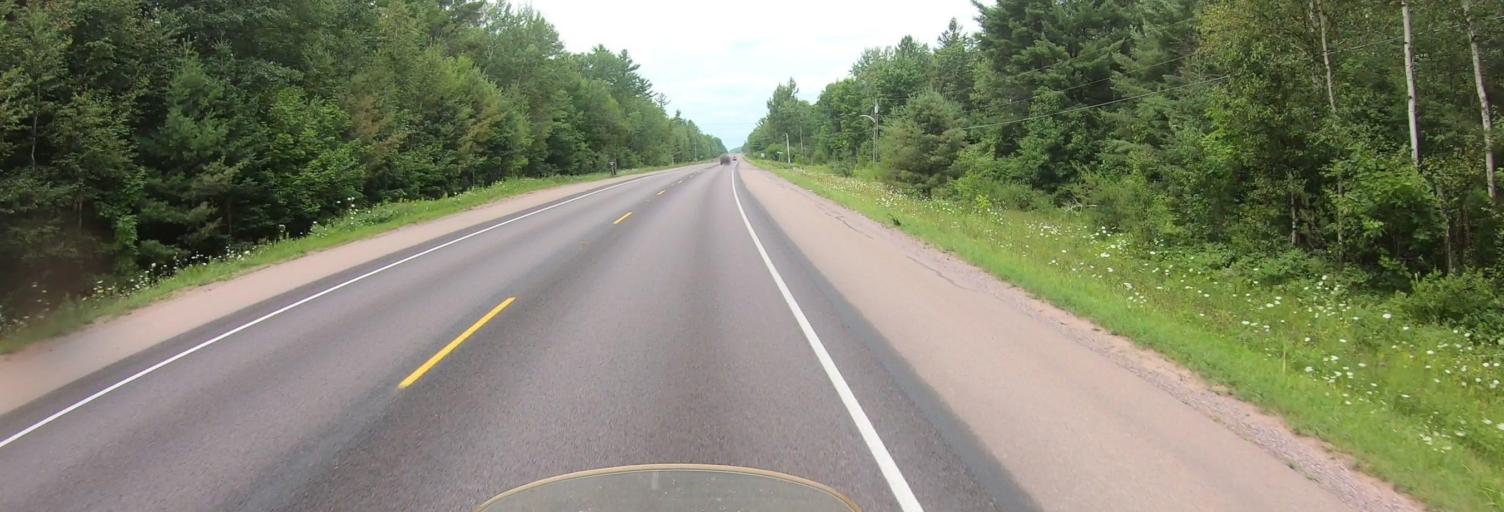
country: US
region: Michigan
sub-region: Marquette County
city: Marquette
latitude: 46.4695
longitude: -87.4390
